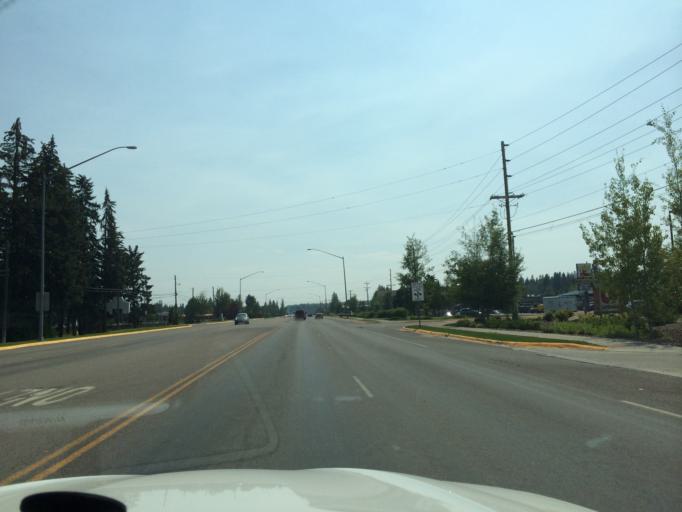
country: US
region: Montana
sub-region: Flathead County
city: Whitefish
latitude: 48.3994
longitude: -114.3351
